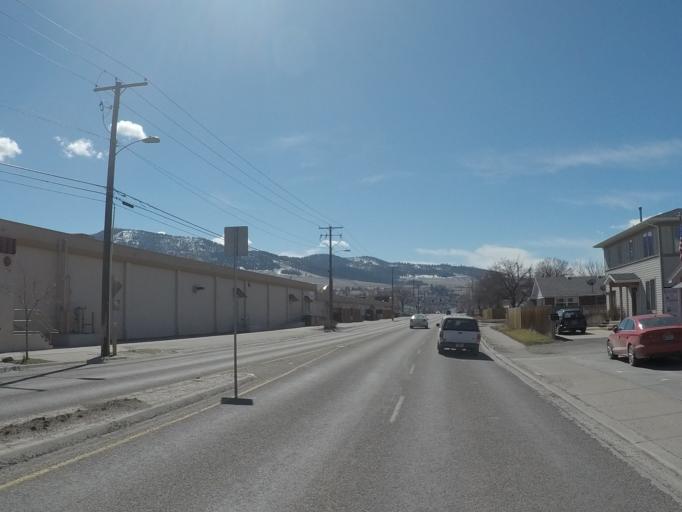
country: US
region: Montana
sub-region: Missoula County
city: Missoula
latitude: 46.8513
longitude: -114.0184
